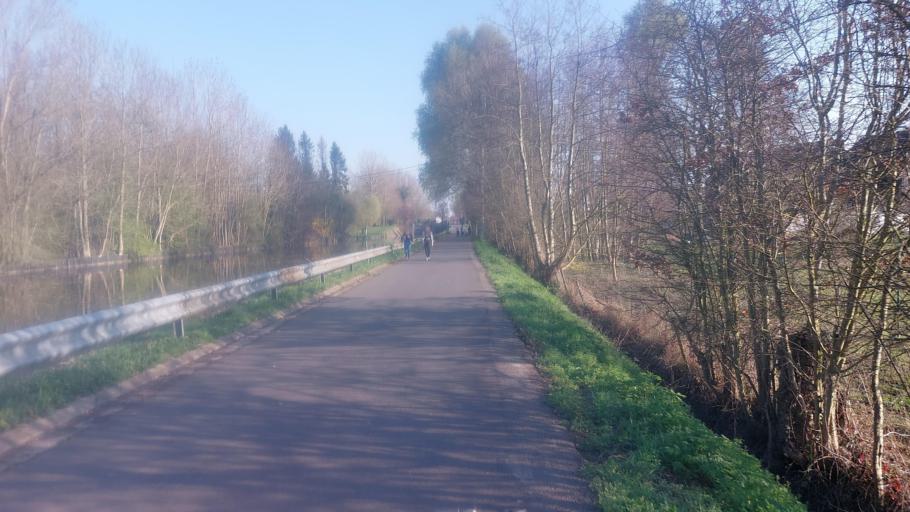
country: BE
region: Wallonia
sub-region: Province du Hainaut
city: Ath
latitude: 50.6223
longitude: 3.7851
